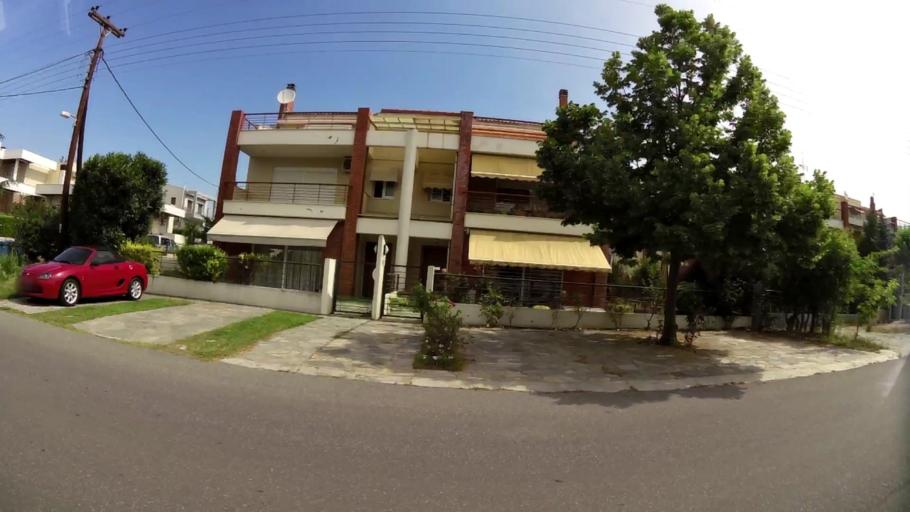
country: GR
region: Central Macedonia
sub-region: Nomos Thessalonikis
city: Panorama
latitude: 40.5806
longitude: 23.0095
